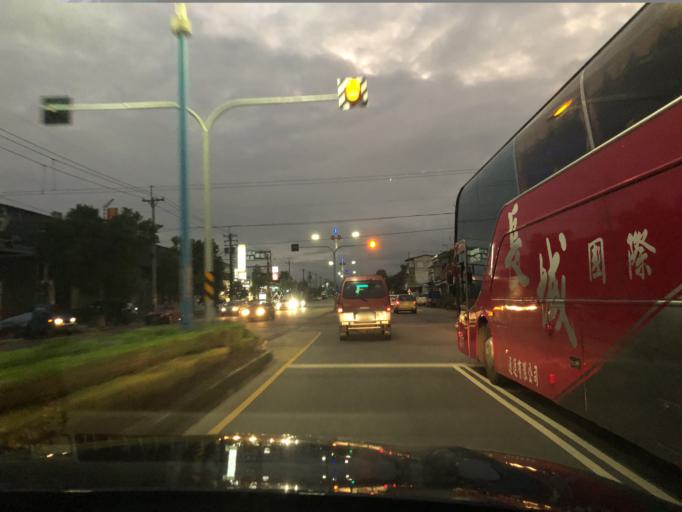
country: TW
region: Taiwan
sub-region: Hualien
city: Hualian
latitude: 23.9728
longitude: 121.5723
